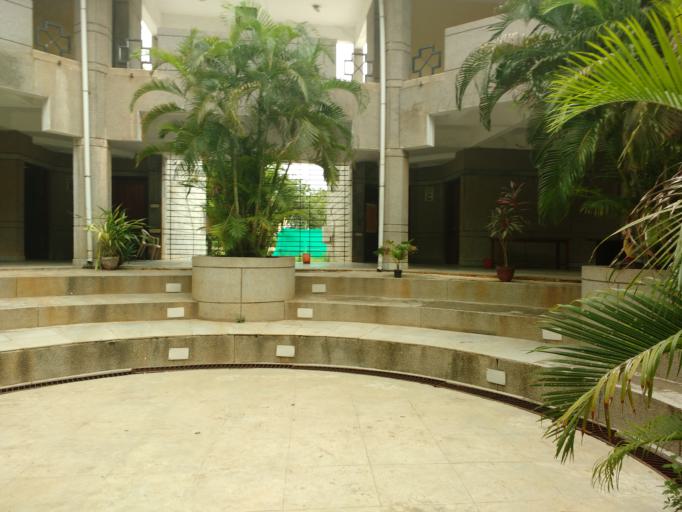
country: IN
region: Tamil Nadu
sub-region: Kancheepuram
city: Sriperumbudur
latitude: 12.9791
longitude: 79.9590
